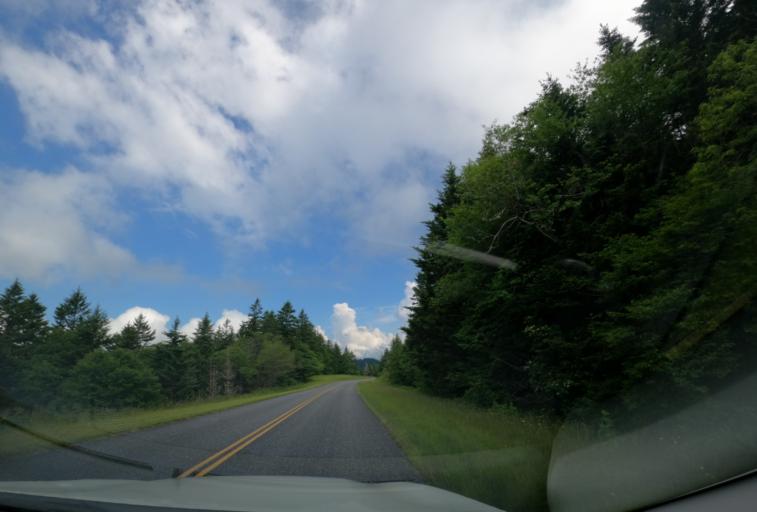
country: US
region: North Carolina
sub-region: Haywood County
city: Hazelwood
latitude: 35.3674
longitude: -82.9965
